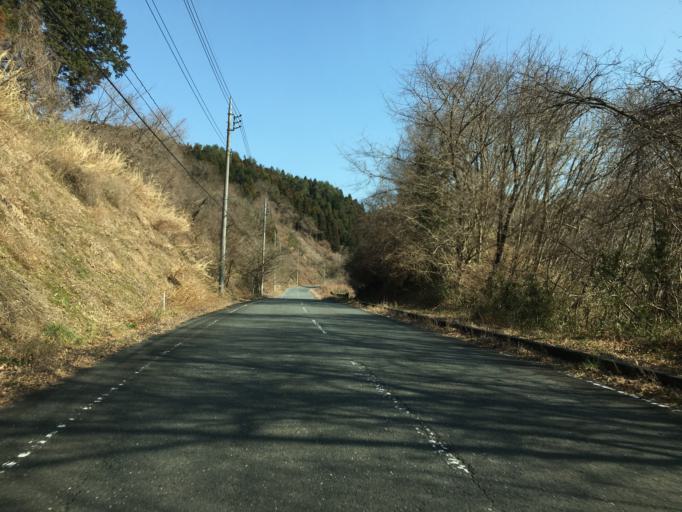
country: JP
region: Ibaraki
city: Kitaibaraki
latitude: 36.8041
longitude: 140.6388
